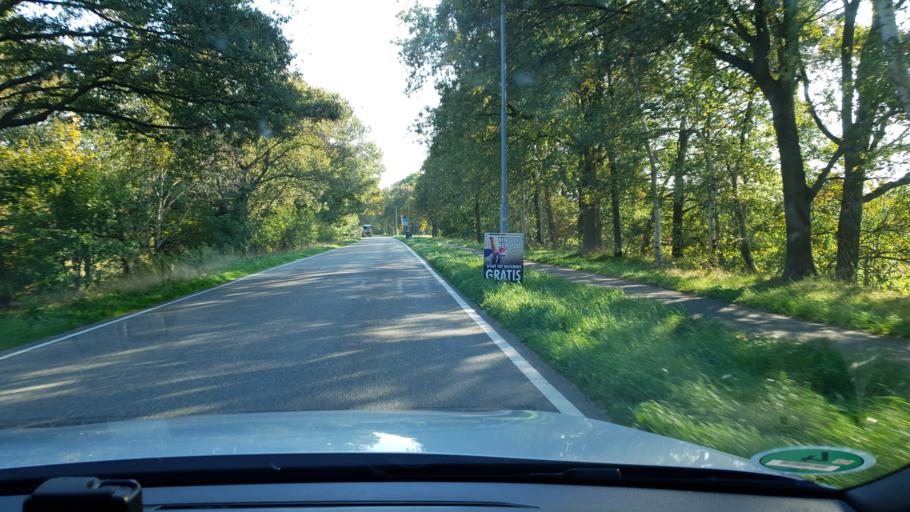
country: NL
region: North Brabant
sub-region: Gemeente Eindhoven
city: Meerhoven
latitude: 51.4699
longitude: 5.3916
